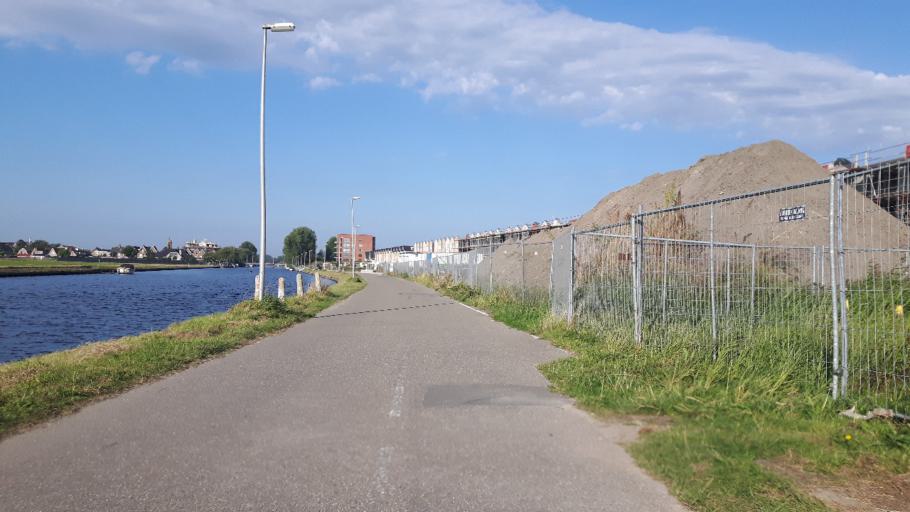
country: NL
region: South Holland
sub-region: Gemeente Katwijk
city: Rijnsburg
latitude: 52.1954
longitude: 4.4543
